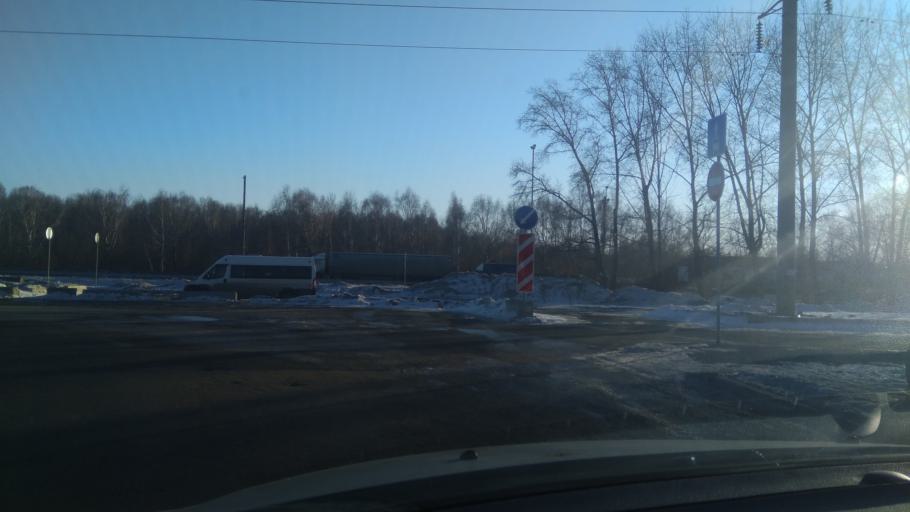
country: RU
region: Sverdlovsk
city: Istok
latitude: 56.8243
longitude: 60.6987
